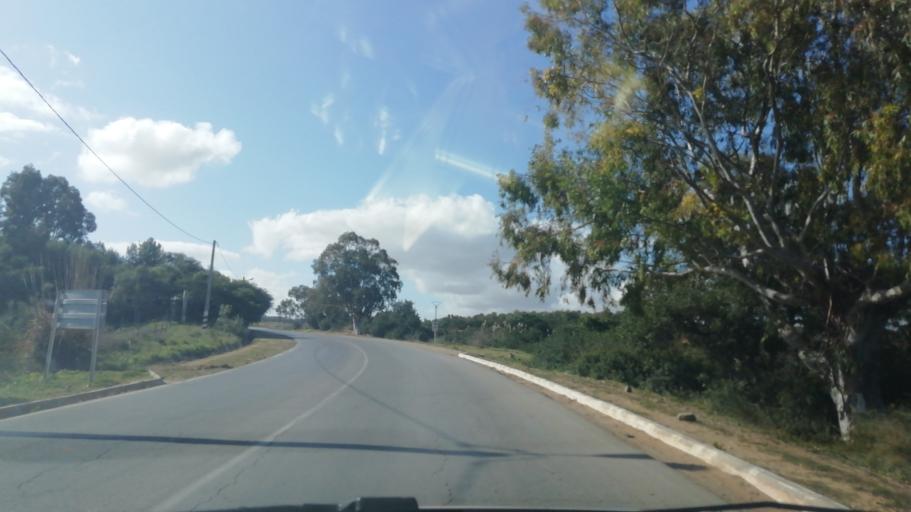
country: DZ
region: Relizane
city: Mazouna
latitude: 36.2952
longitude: 0.6566
